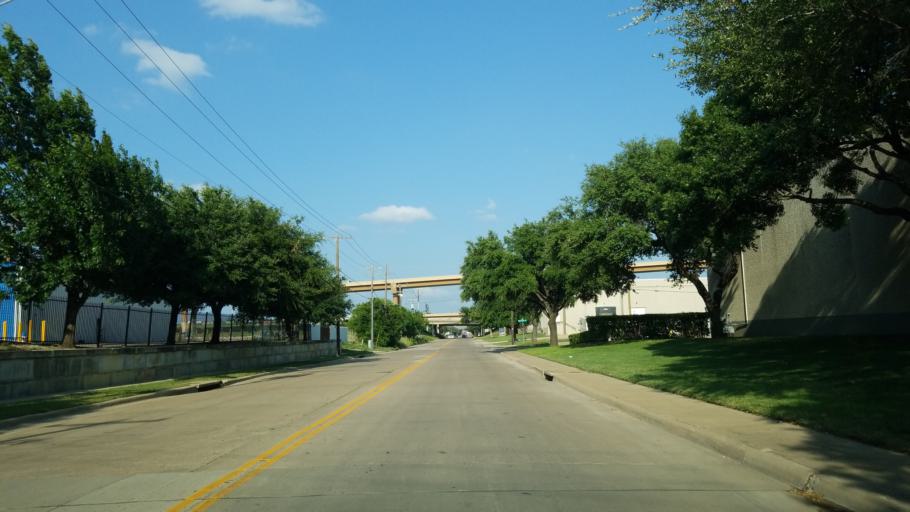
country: US
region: Texas
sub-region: Dallas County
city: Farmers Branch
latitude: 32.8739
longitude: -96.9011
